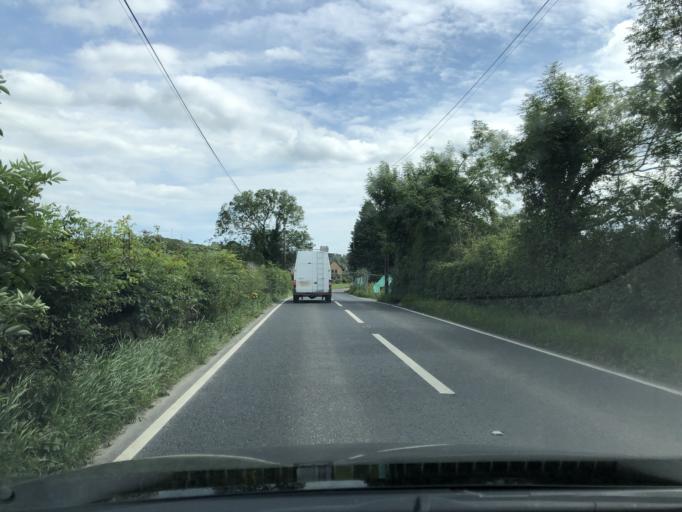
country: GB
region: Northern Ireland
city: Ballynahinch
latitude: 54.4140
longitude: -5.9049
